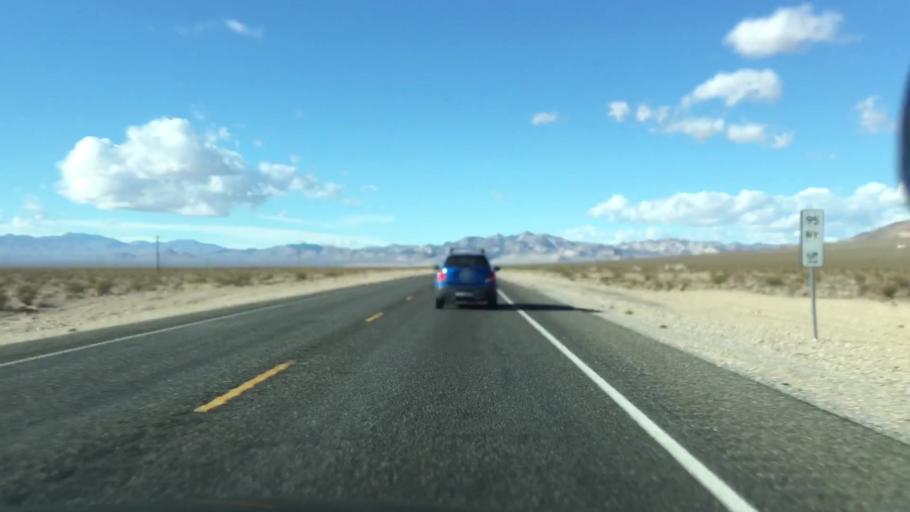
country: US
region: Nevada
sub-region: Nye County
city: Beatty
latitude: 36.7958
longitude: -116.7111
